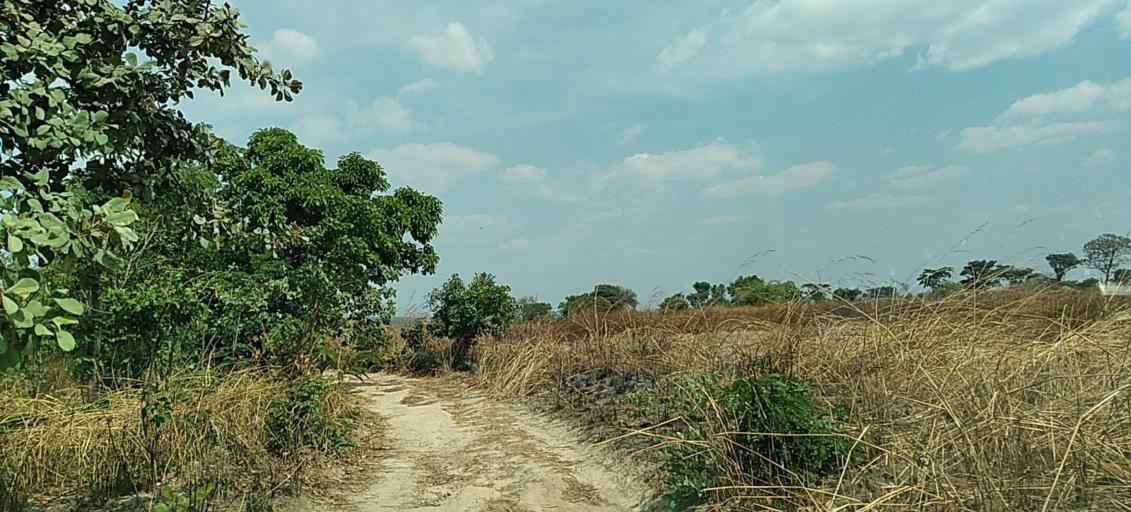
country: ZM
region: Copperbelt
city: Chililabombwe
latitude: -12.3430
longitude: 27.7871
